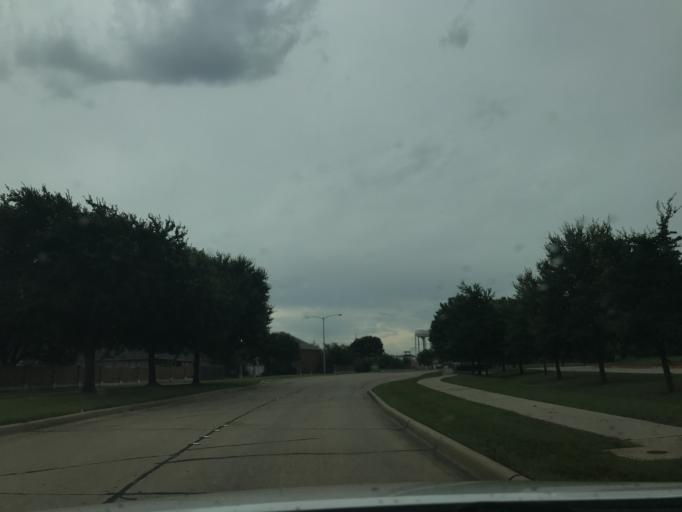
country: US
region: Texas
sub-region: Denton County
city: Lewisville
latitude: 33.0518
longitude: -97.0146
